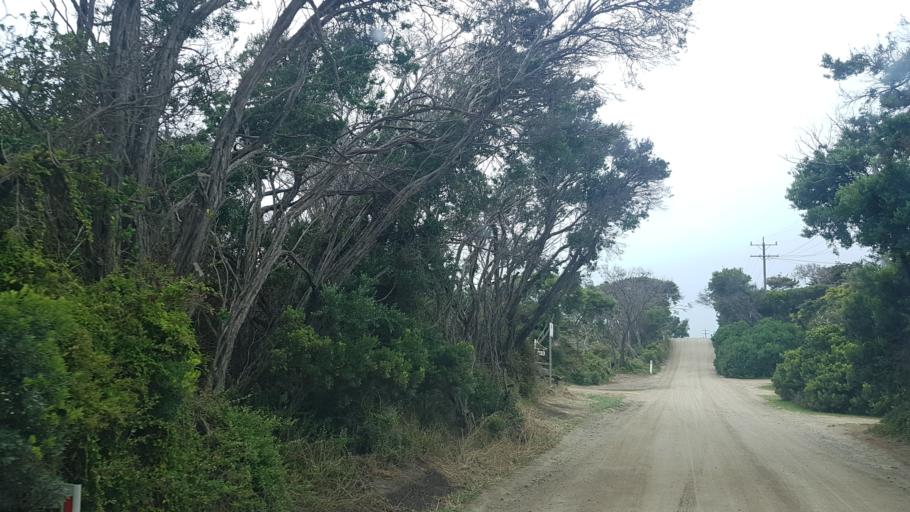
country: AU
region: Victoria
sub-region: Mornington Peninsula
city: Blairgowrie
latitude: -38.3719
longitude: 144.7674
